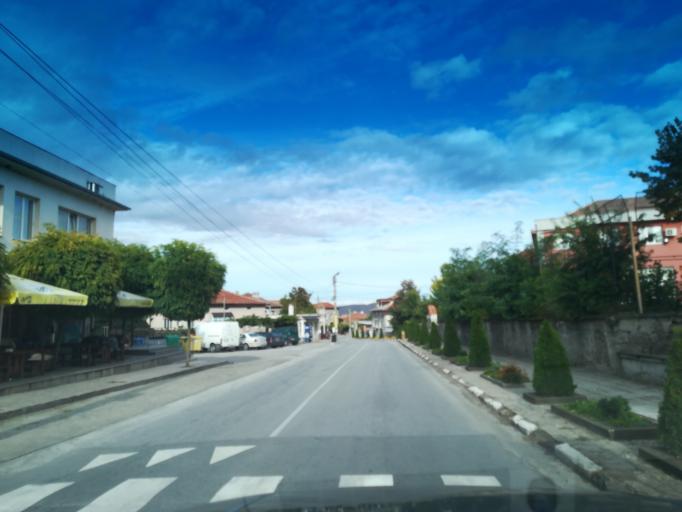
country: BG
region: Pazardzhik
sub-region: Obshtina Bratsigovo
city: Bratsigovo
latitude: 42.0659
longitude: 24.3770
